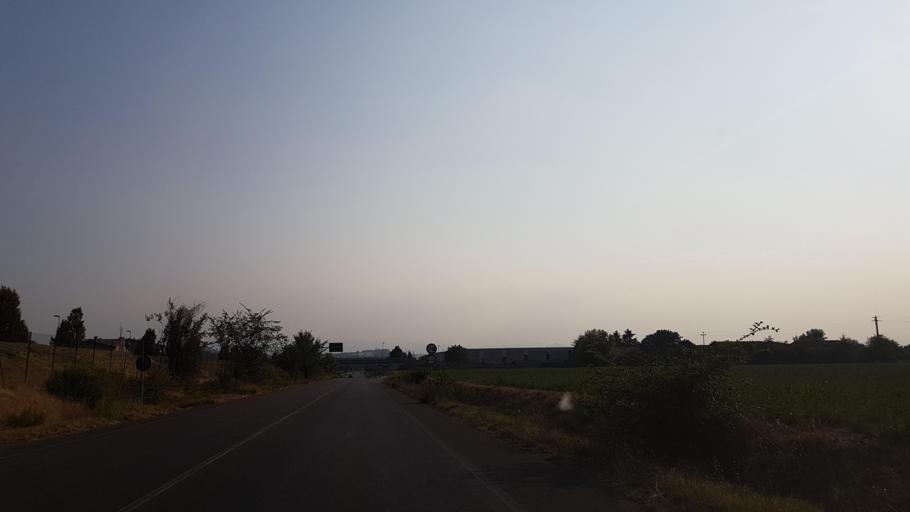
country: IT
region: Emilia-Romagna
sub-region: Provincia di Parma
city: Collecchio
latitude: 44.7573
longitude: 10.2026
